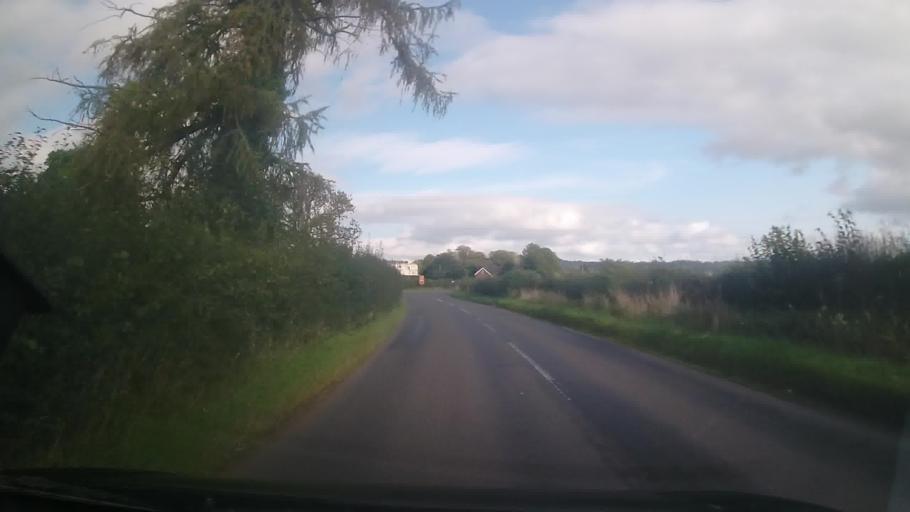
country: GB
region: England
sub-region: Shropshire
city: Craven Arms
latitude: 52.4305
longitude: -2.9010
